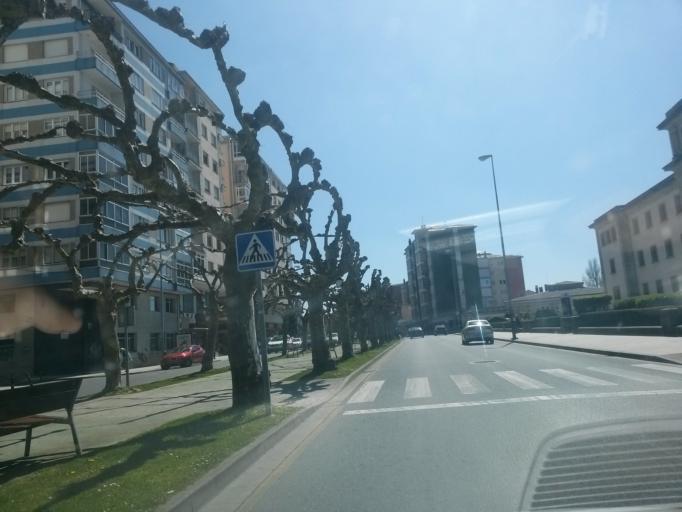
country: ES
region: Galicia
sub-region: Provincia de Lugo
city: Lugo
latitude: 43.0058
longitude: -7.5556
